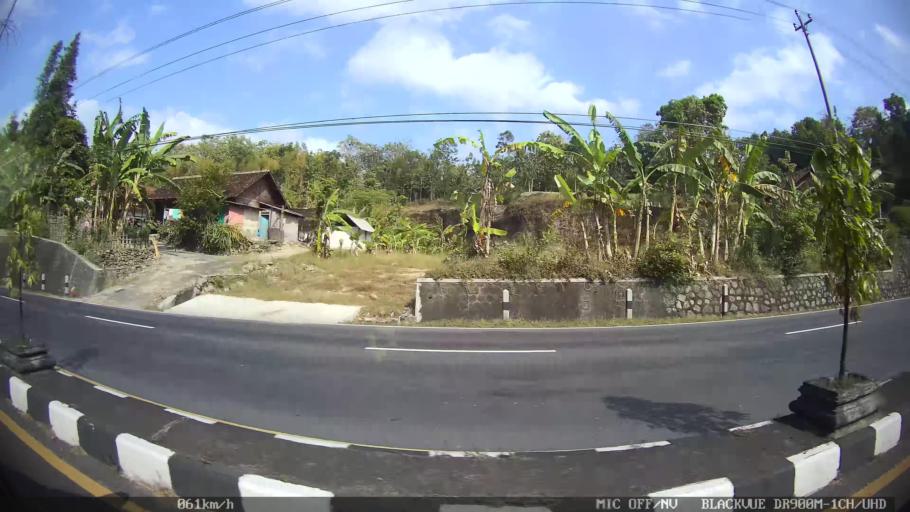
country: ID
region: Daerah Istimewa Yogyakarta
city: Srandakan
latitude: -7.8518
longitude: 110.2166
